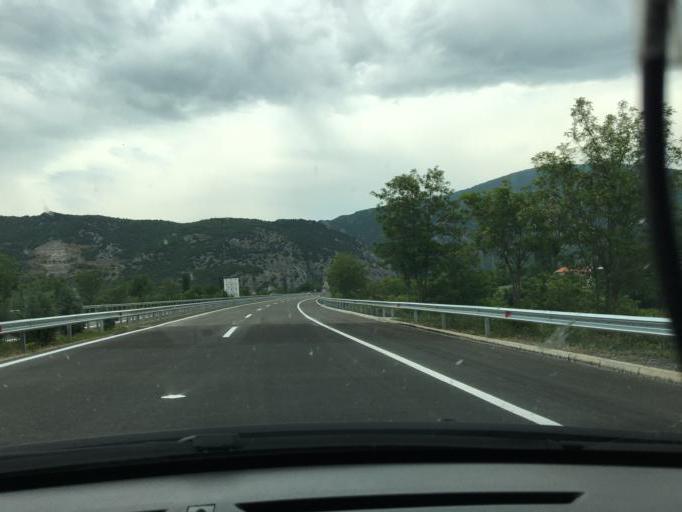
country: MK
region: Demir Kapija
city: Demir Kapija
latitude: 41.4149
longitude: 22.2413
